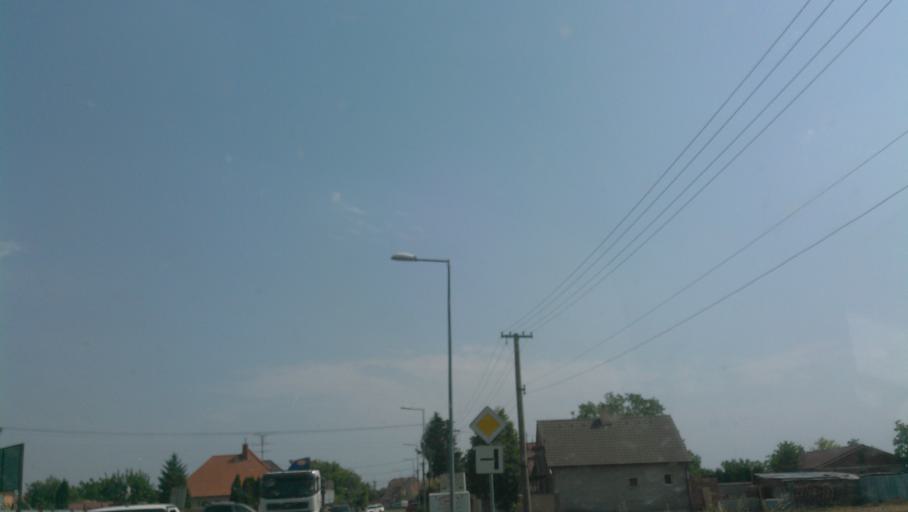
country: SK
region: Trnavsky
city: Samorin
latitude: 48.0585
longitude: 17.4406
